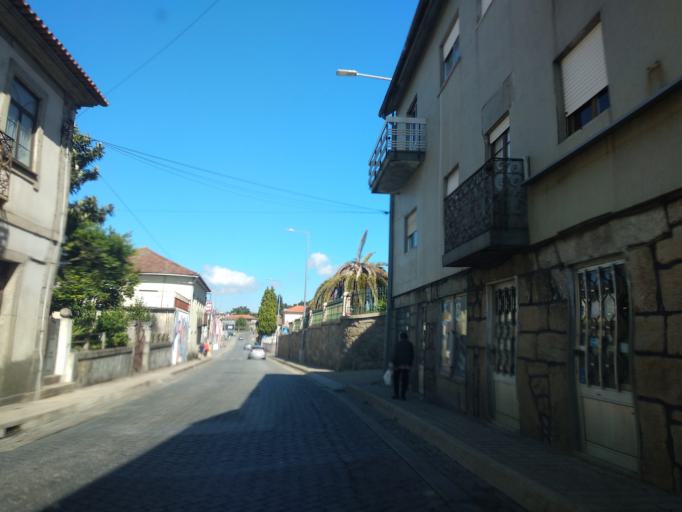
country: PT
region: Porto
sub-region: Pacos de Ferreira
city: Freamunde
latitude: 41.2867
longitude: -8.3347
